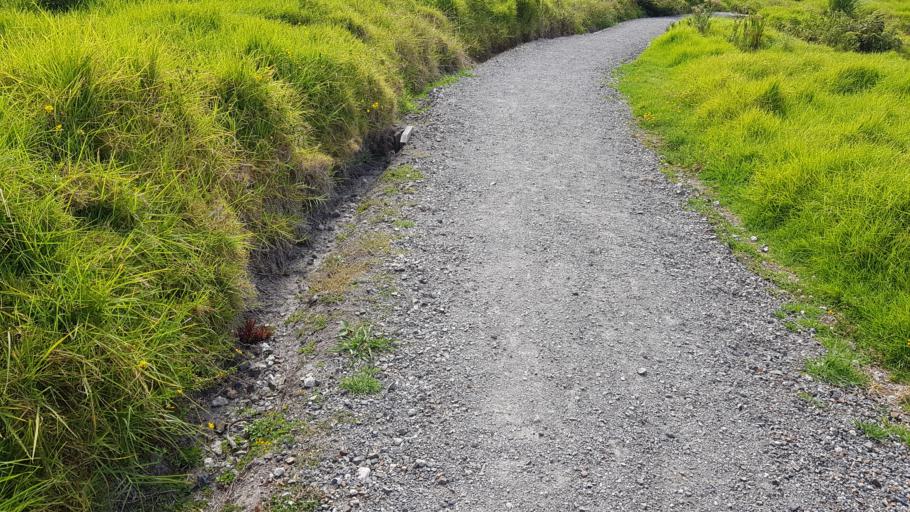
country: NZ
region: Auckland
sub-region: Auckland
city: Rothesay Bay
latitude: -36.6705
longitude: 174.7463
